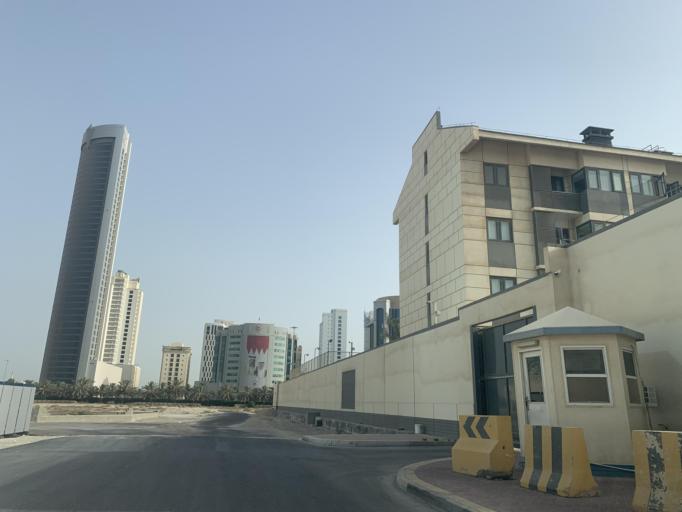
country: BH
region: Manama
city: Jidd Hafs
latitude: 26.2339
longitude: 50.5467
